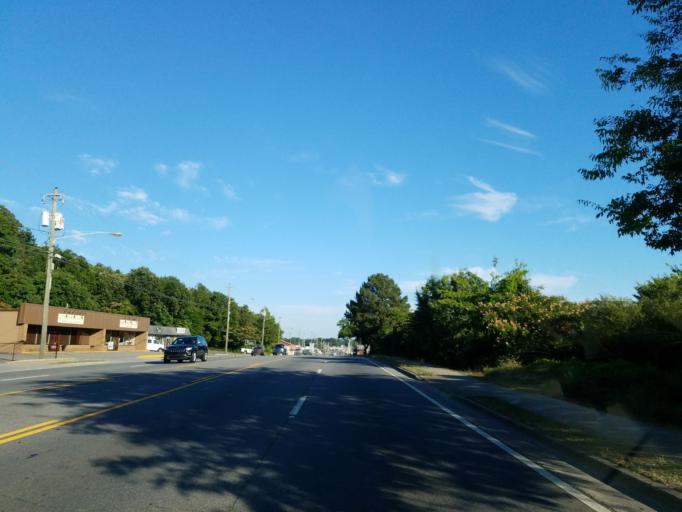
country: US
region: Georgia
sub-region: Gordon County
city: Calhoun
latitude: 34.4943
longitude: -84.9505
